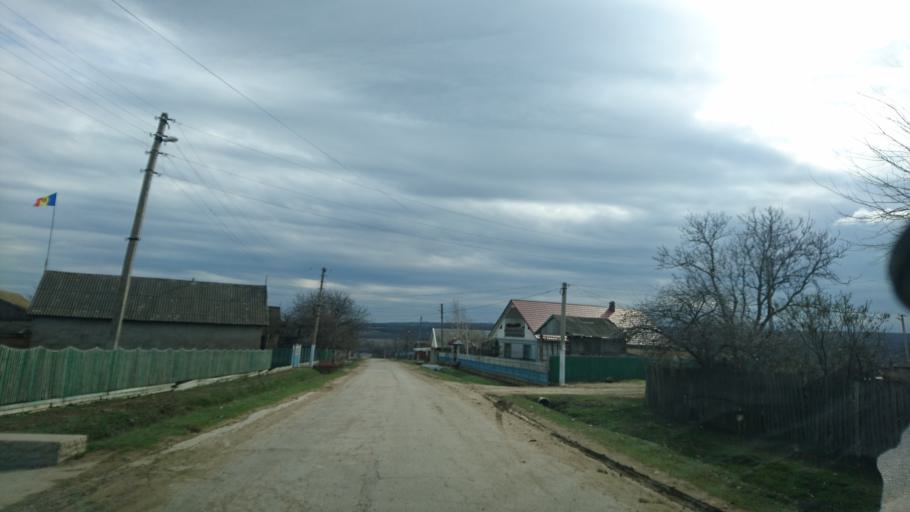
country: MD
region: Cantemir
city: Visniovca
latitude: 46.3341
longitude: 28.4020
